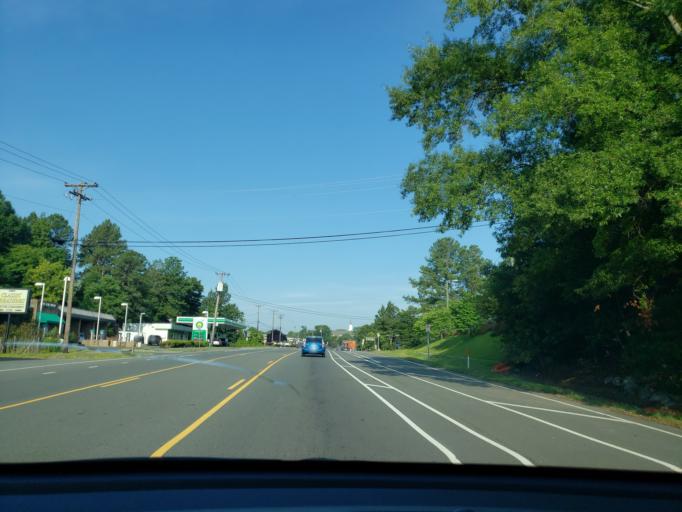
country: US
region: North Carolina
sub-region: Durham County
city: Durham
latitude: 35.9743
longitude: -78.9297
